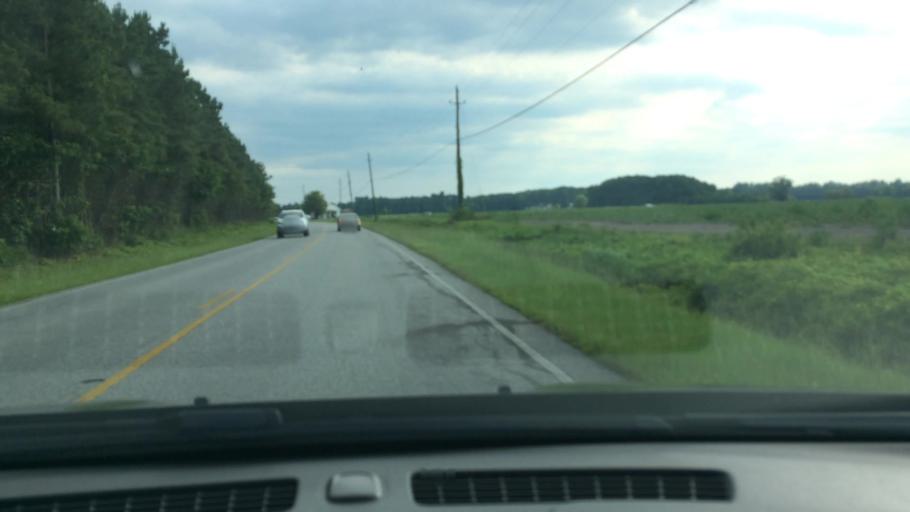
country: US
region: North Carolina
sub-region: Pitt County
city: Ayden
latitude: 35.4732
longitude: -77.3831
